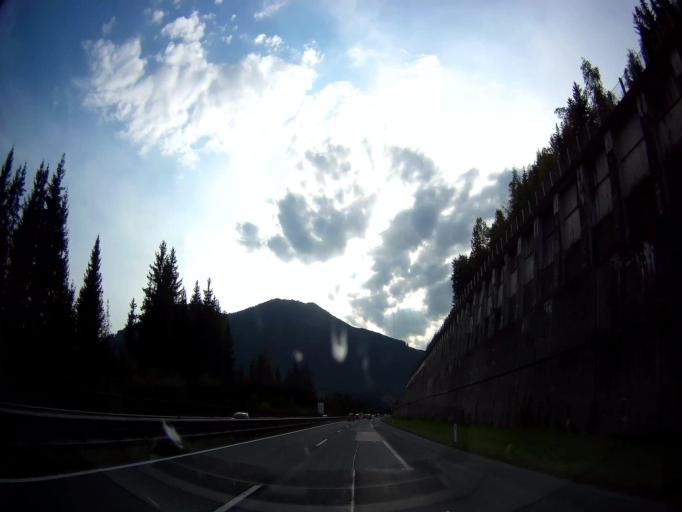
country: AT
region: Salzburg
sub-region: Politischer Bezirk Sankt Johann im Pongau
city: Huttau
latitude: 47.4218
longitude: 13.3256
